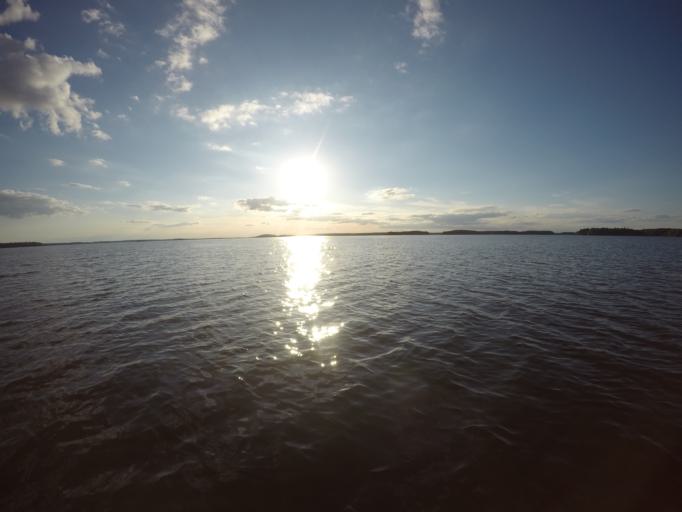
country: SE
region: Soedermanland
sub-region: Eskilstuna Kommun
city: Kvicksund
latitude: 59.4502
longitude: 16.2401
